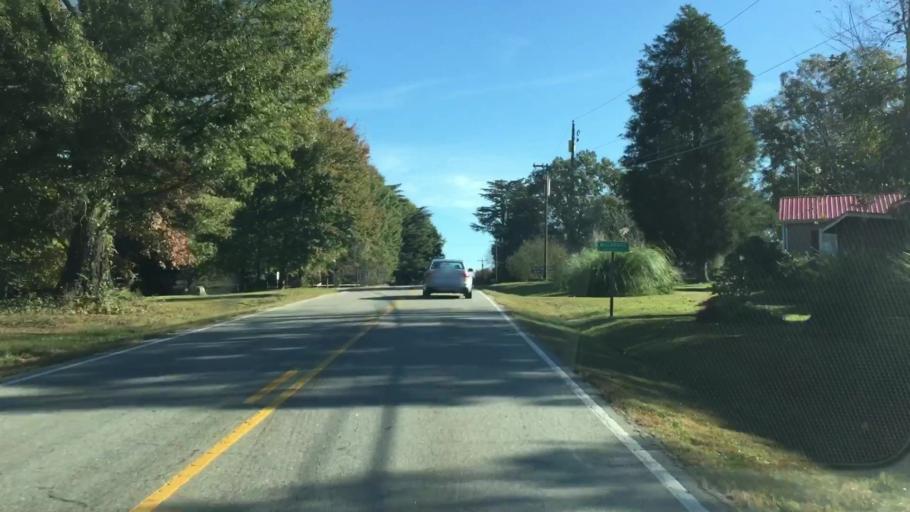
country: US
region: North Carolina
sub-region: Rowan County
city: China Grove
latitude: 35.6465
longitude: -80.6389
